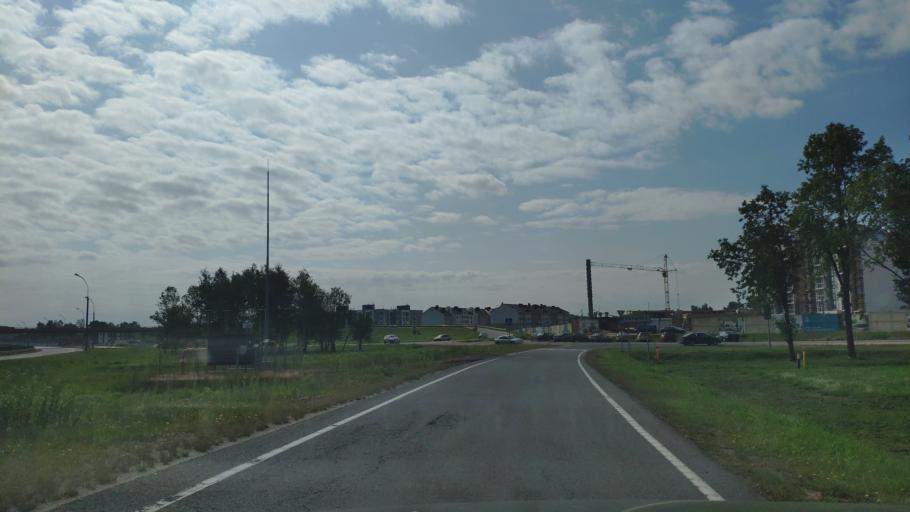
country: BY
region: Minsk
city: Khatsyezhyna
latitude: 53.9497
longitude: 27.3330
